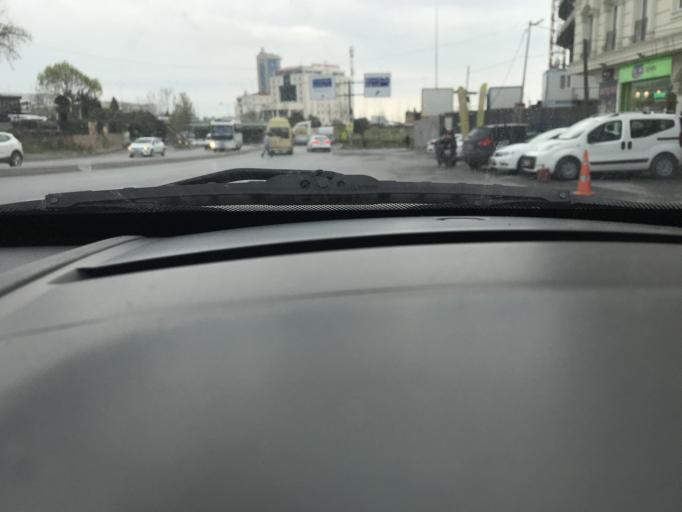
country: TR
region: Istanbul
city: Yakuplu
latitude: 41.0013
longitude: 28.6989
